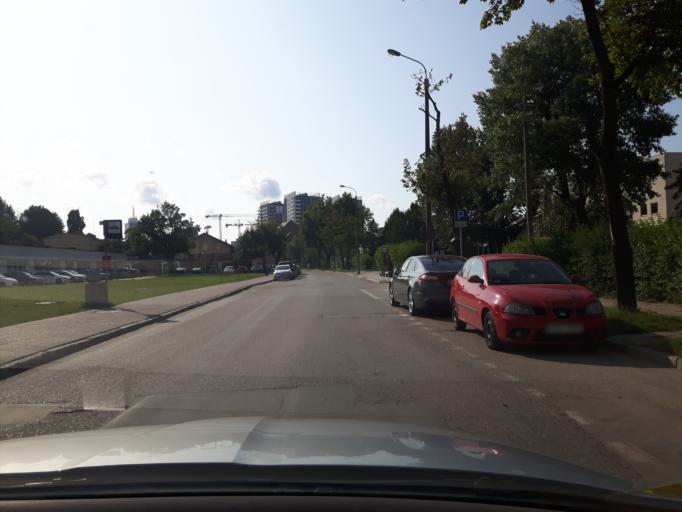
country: PL
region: Pomeranian Voivodeship
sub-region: Gdansk
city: Gdansk
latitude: 54.3574
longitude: 18.6596
